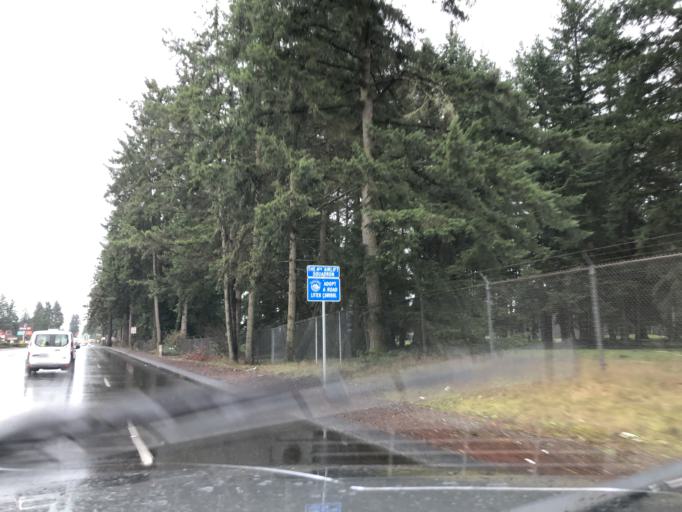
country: US
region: Washington
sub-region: Pierce County
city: Spanaway
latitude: 47.1206
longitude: -122.4390
